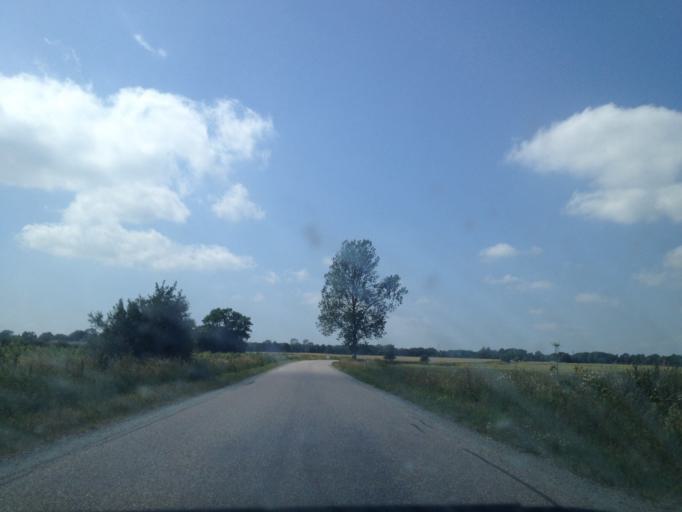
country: DK
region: South Denmark
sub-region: Kolding Kommune
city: Vamdrup
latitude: 55.3851
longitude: 9.2628
